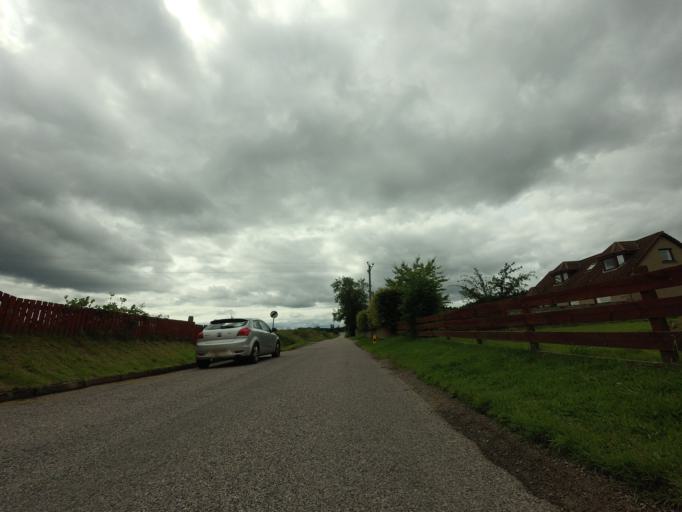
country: GB
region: Scotland
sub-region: Moray
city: Forres
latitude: 57.6022
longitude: -3.6936
